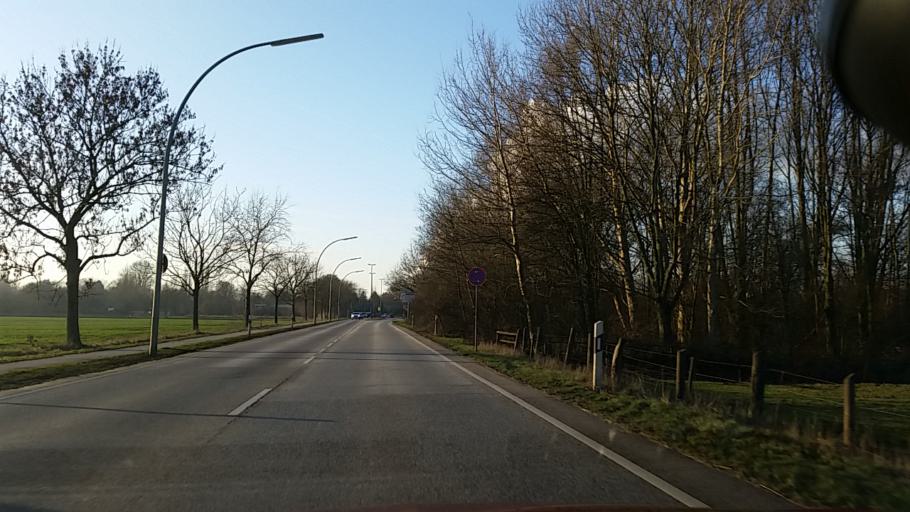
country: DE
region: Hamburg
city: Harburg
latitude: 53.4802
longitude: 10.0123
